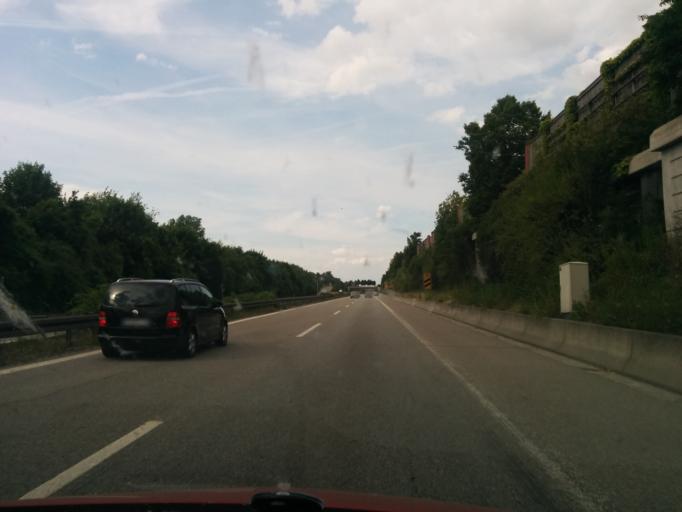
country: DE
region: Bavaria
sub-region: Swabia
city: Klosterlechfeld
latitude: 48.1687
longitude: 10.8376
